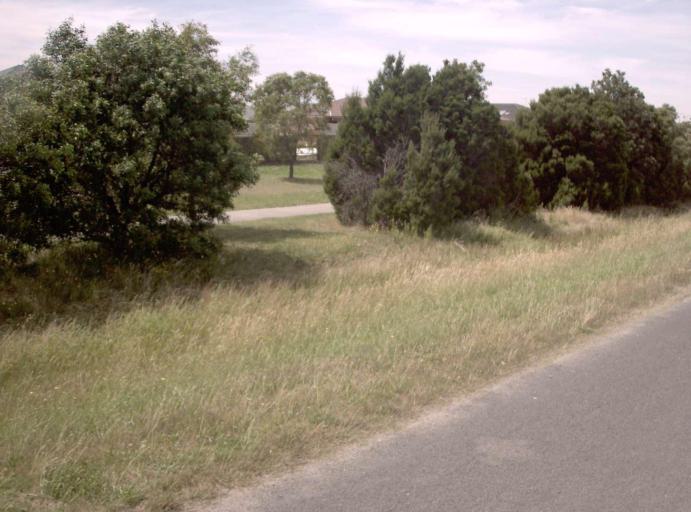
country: AU
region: Victoria
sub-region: Casey
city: Lynbrook
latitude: -38.0731
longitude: 145.2405
